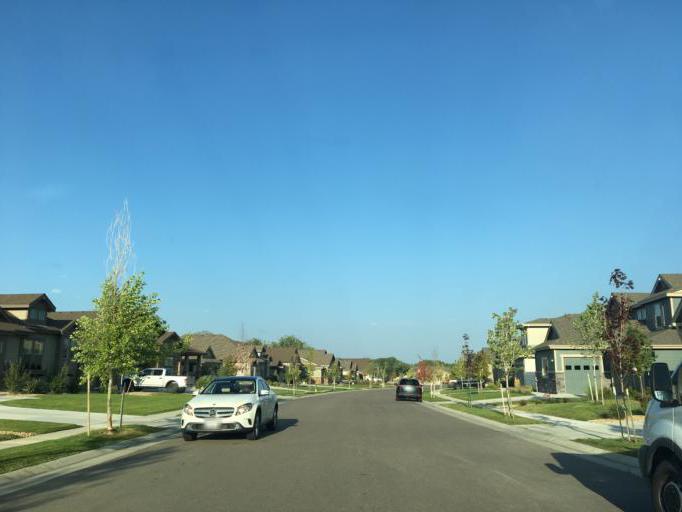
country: US
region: Colorado
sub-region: Jefferson County
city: Applewood
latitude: 39.7892
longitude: -105.1732
